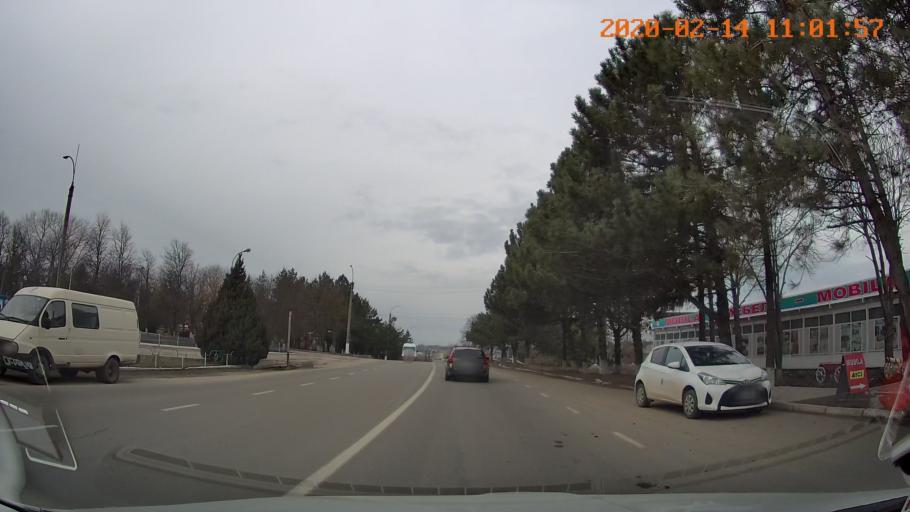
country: MD
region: Raionul Edinet
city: Edinet
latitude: 48.1625
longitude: 27.3245
